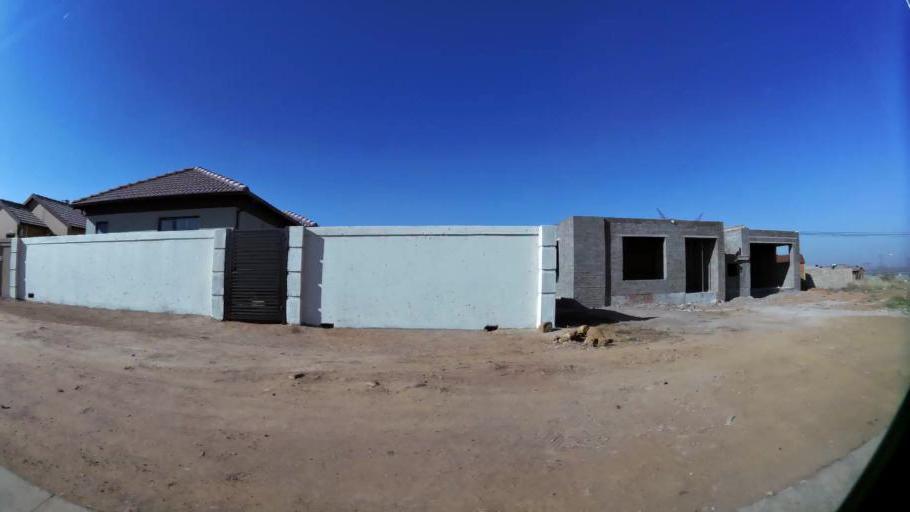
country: ZA
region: Gauteng
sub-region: City of Tshwane Metropolitan Municipality
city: Mabopane
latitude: -25.5597
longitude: 28.0967
